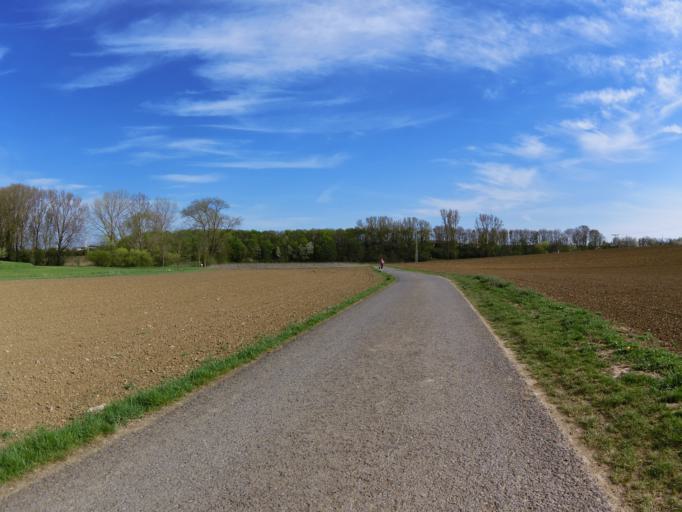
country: DE
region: Bavaria
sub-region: Regierungsbezirk Unterfranken
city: Unterpleichfeld
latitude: 49.8667
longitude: 10.0291
